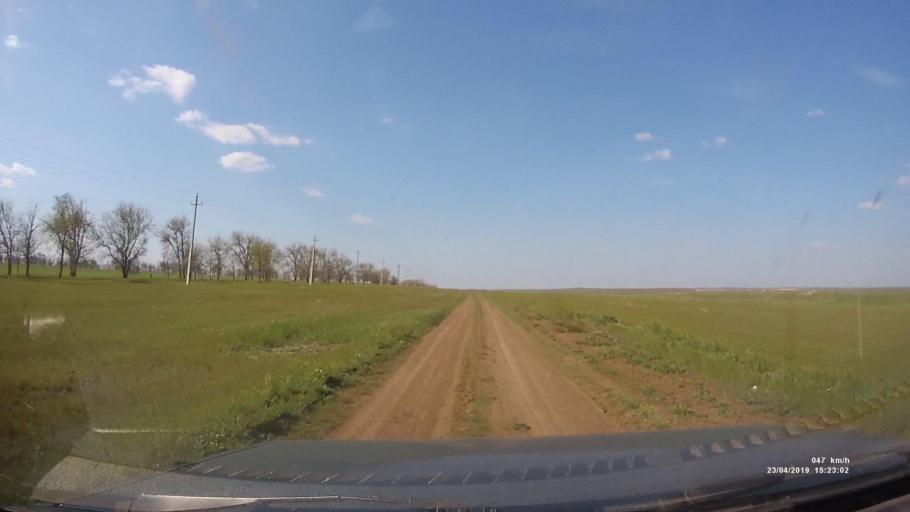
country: RU
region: Rostov
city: Remontnoye
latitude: 46.5329
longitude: 42.9698
